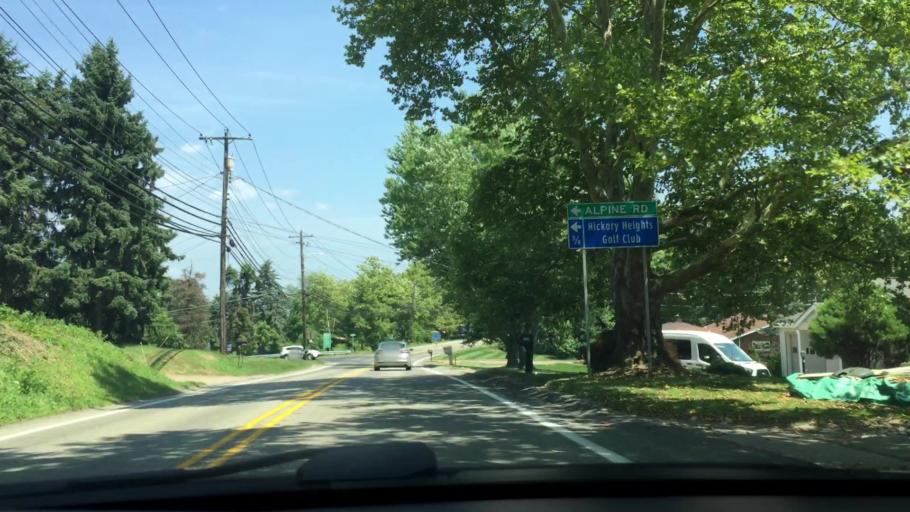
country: US
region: Pennsylvania
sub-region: Allegheny County
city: Bridgeville
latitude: 40.3350
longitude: -80.1329
